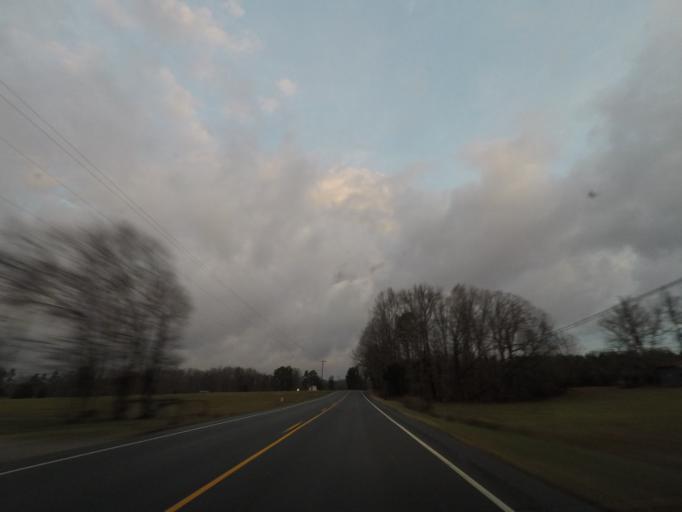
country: US
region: North Carolina
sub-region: Orange County
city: Hillsborough
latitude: 36.1873
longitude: -79.1379
